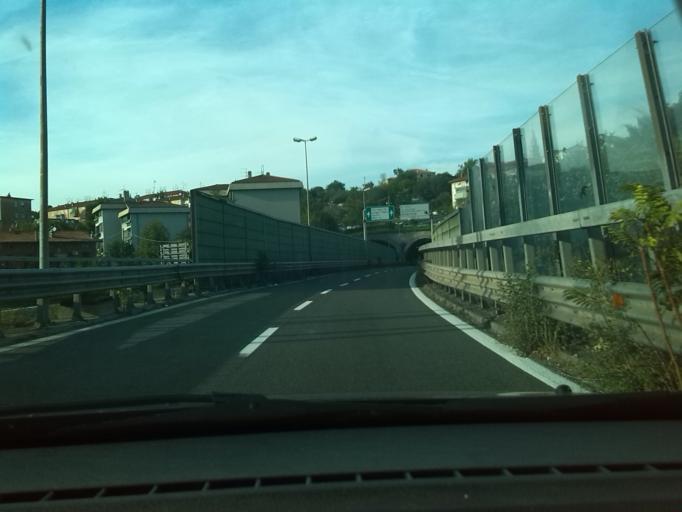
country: IT
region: Friuli Venezia Giulia
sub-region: Provincia di Trieste
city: Muggia
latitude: 45.6226
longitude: 13.7808
